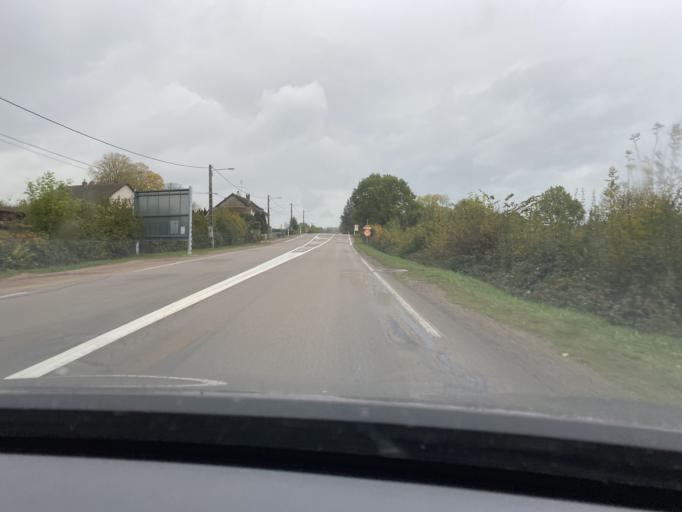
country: FR
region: Bourgogne
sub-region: Departement de la Cote-d'Or
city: Saulieu
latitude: 47.2872
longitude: 4.2243
